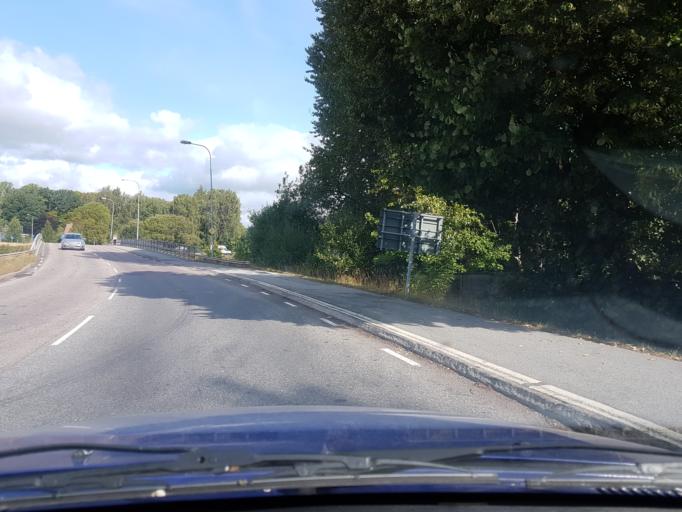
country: SE
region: Vaestra Goetaland
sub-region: Lerums Kommun
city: Stenkullen
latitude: 57.8019
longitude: 12.3686
